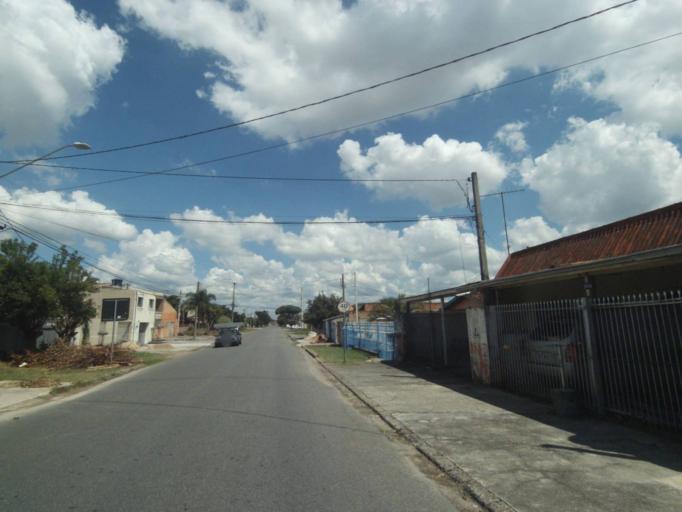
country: BR
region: Parana
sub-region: Pinhais
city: Pinhais
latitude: -25.4452
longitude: -49.2037
